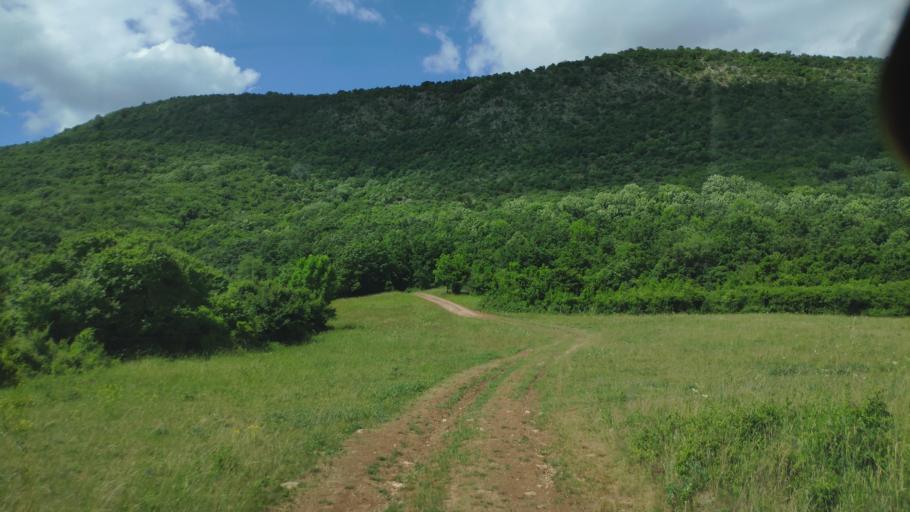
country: SK
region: Kosicky
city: Medzev
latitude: 48.6242
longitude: 20.8755
